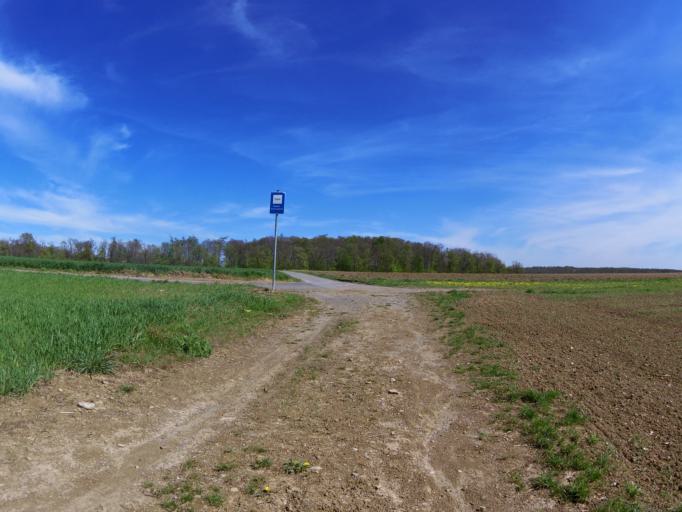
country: DE
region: Bavaria
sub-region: Regierungsbezirk Unterfranken
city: Rimpar
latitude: 49.8584
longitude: 9.9751
